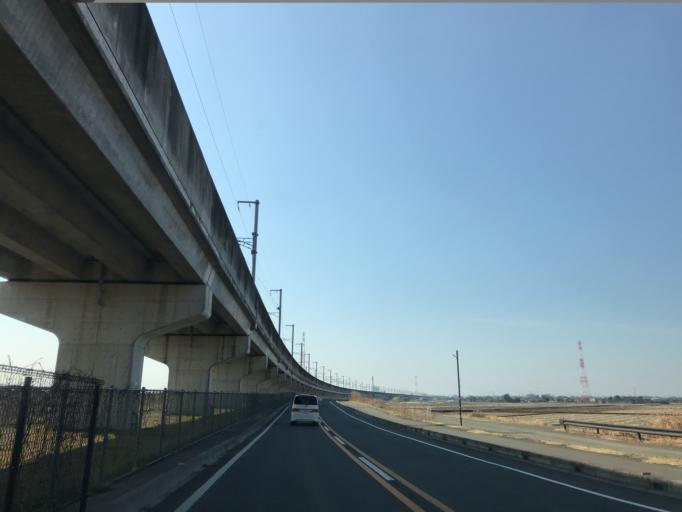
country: JP
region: Ibaraki
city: Mitsukaido
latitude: 35.9879
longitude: 140.0343
